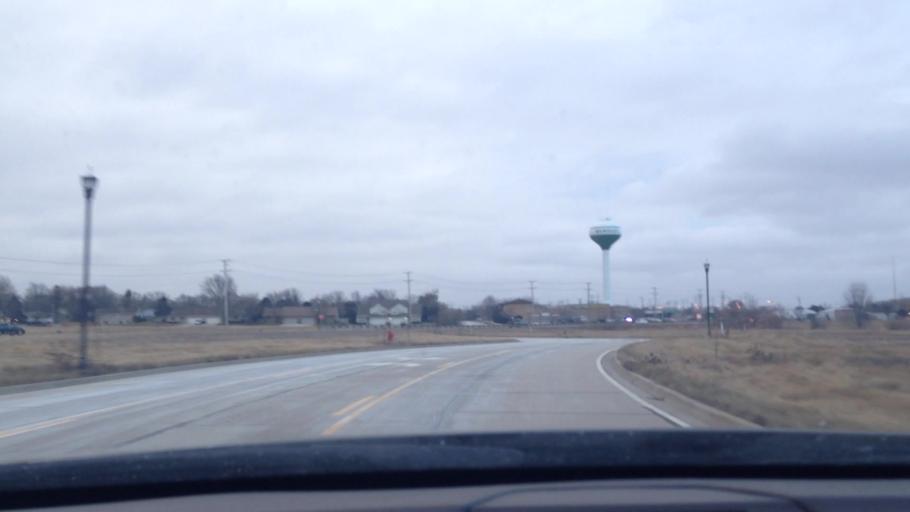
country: US
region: Illinois
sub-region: McHenry County
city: Huntley
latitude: 42.1824
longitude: -88.4247
